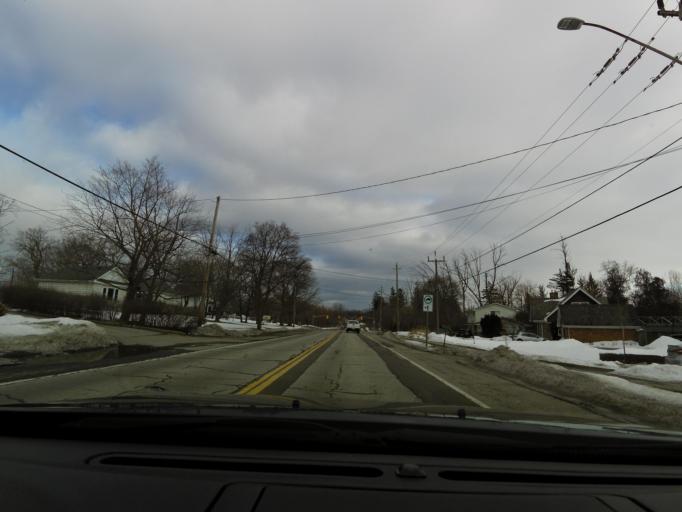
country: CA
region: Ontario
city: Hamilton
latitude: 43.2072
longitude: -79.6426
